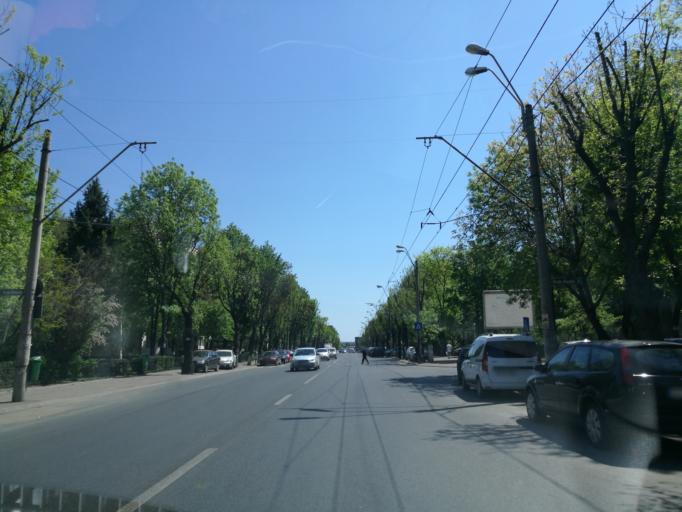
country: RO
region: Ilfov
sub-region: Comuna Popesti-Leordeni
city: Popesti-Leordeni
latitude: 44.3830
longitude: 26.1241
